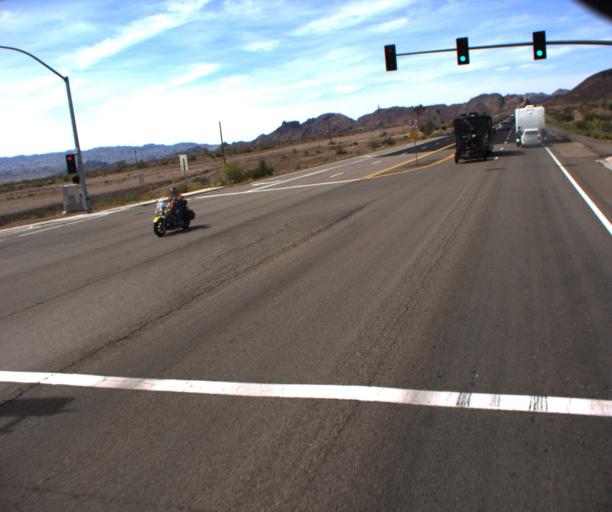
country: US
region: Arizona
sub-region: Mohave County
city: Desert Hills
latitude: 34.5790
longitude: -114.3668
